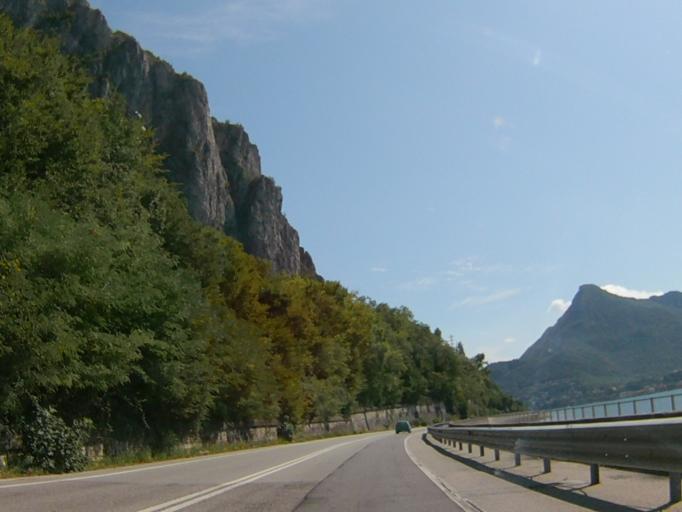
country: IT
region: Lombardy
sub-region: Provincia di Lecco
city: Lecco
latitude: 45.8746
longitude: 9.3771
